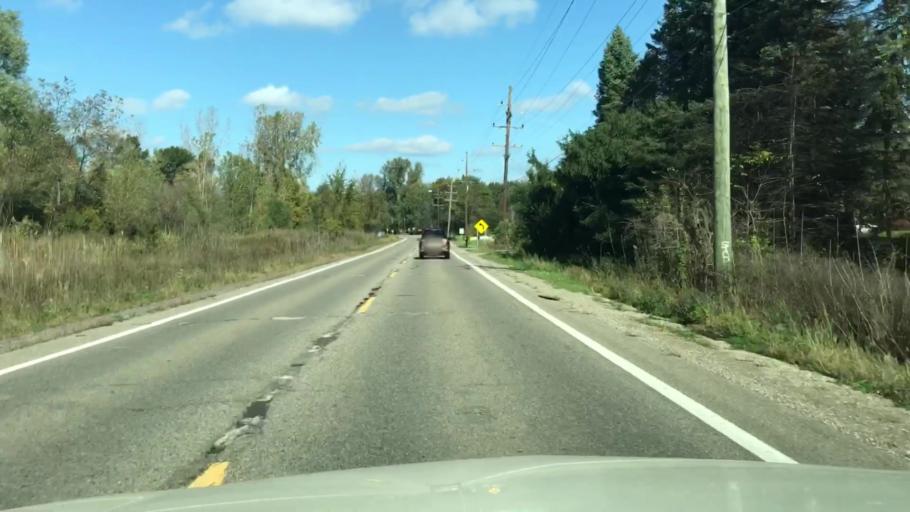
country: US
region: Michigan
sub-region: Oakland County
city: Rochester
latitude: 42.6660
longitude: -83.0934
